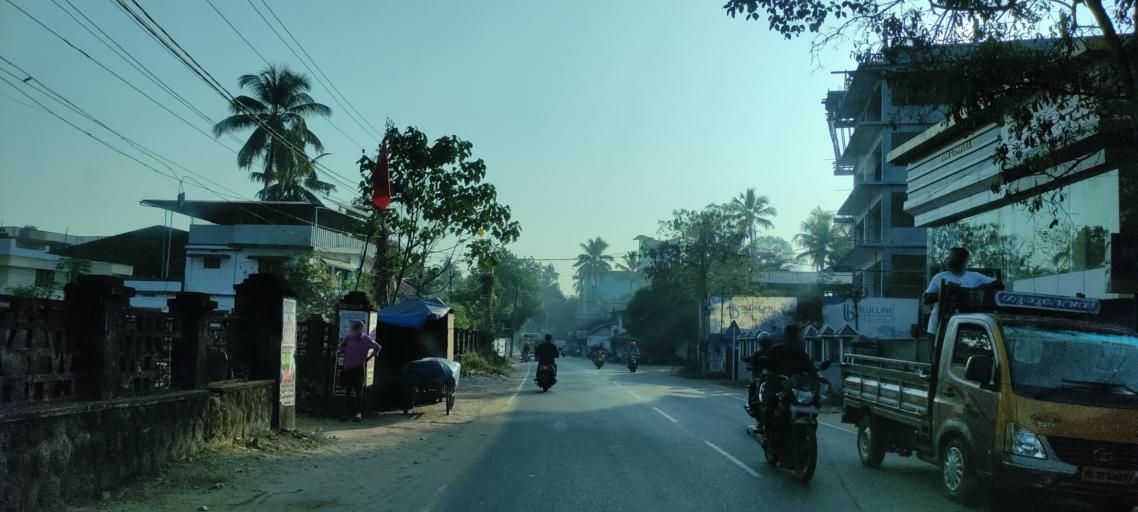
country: IN
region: Kerala
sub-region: Alappuzha
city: Kayankulam
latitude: 9.1755
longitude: 76.5110
